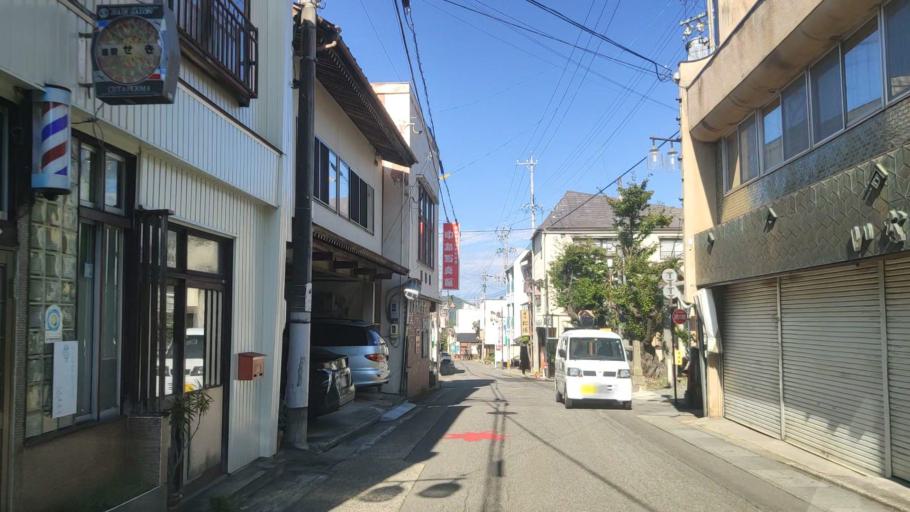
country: JP
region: Nagano
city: Nakano
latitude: 36.7409
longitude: 138.4176
